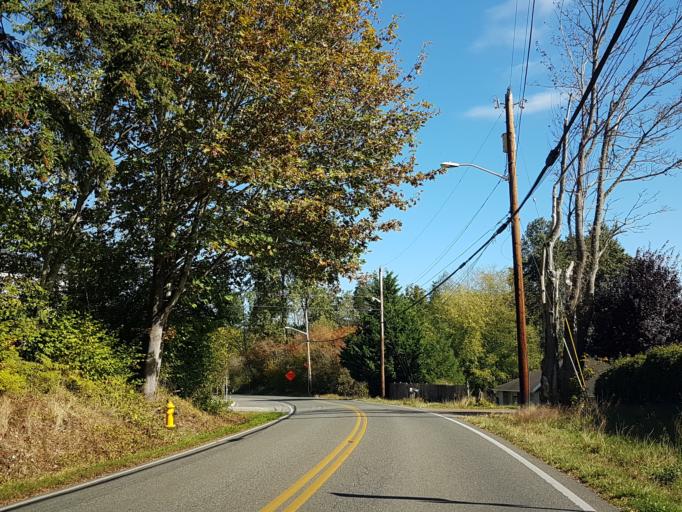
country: US
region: Washington
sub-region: Snohomish County
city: Brier
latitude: 47.7791
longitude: -122.2584
